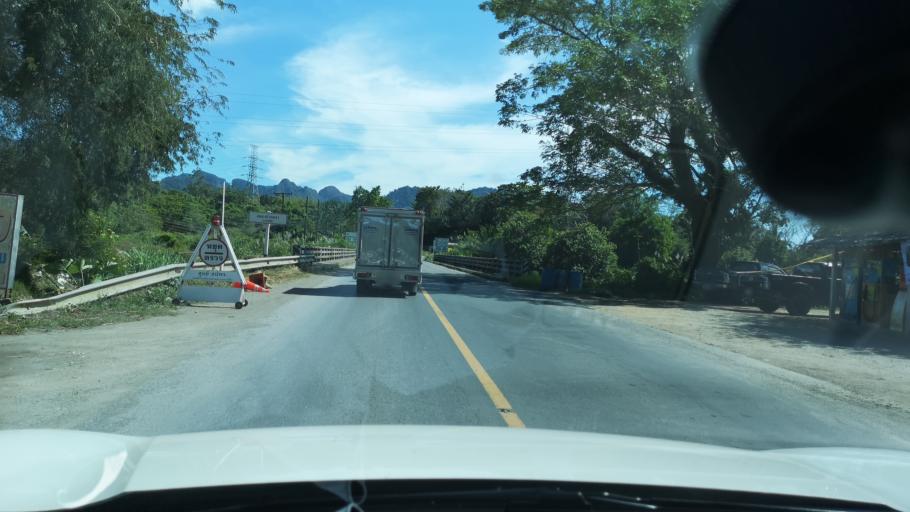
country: TH
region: Phangnga
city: Phang Nga
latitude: 8.5297
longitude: 98.5166
